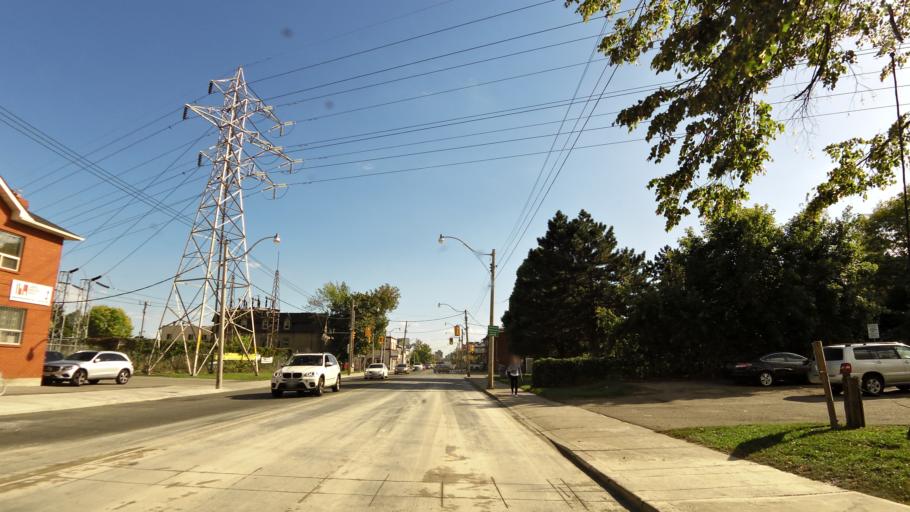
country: CA
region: Ontario
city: Toronto
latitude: 43.6709
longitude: -79.4402
